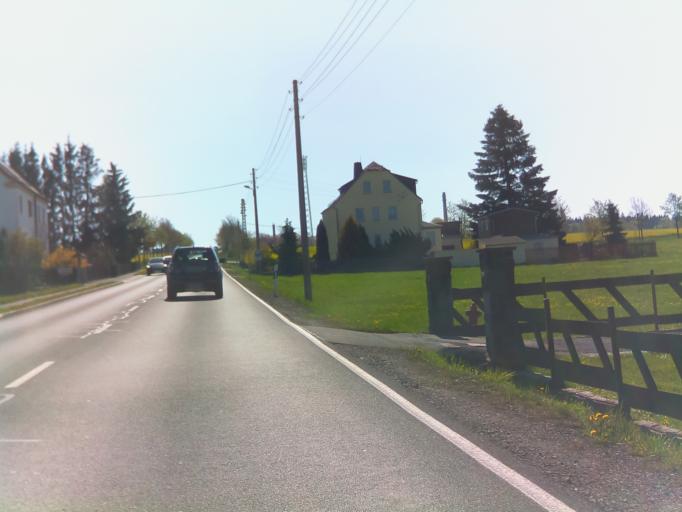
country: DE
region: Saxony
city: Mehltheuer
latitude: 50.5470
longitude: 12.0244
